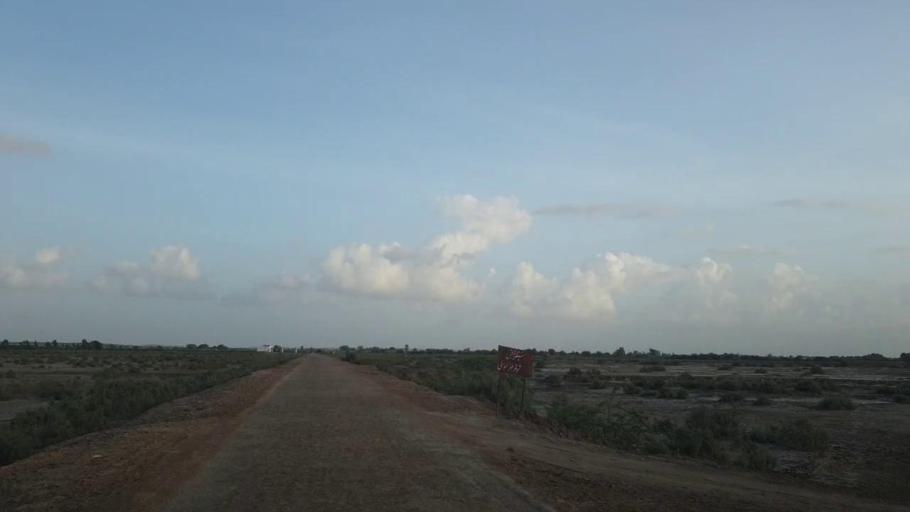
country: PK
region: Sindh
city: Kadhan
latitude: 24.5529
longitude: 69.1235
